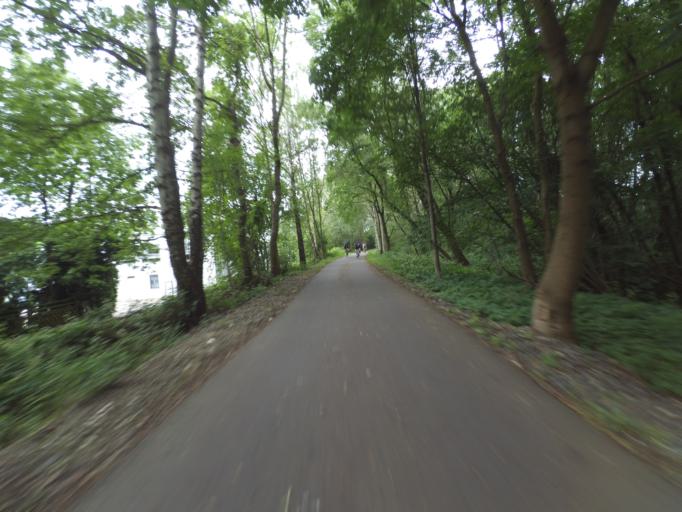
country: DE
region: North Rhine-Westphalia
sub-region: Regierungsbezirk Koln
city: Wurselen
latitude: 50.7571
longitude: 6.1579
